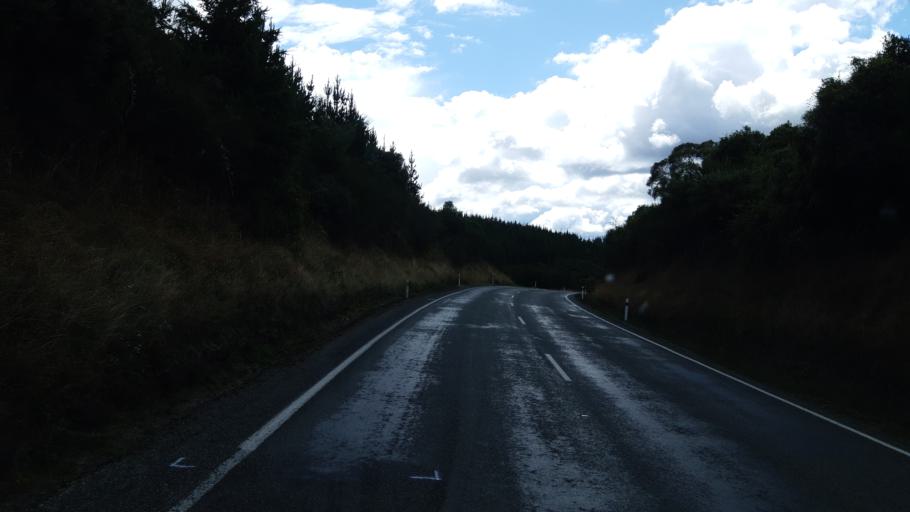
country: NZ
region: Tasman
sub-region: Tasman District
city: Wakefield
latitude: -41.5523
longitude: 172.7899
